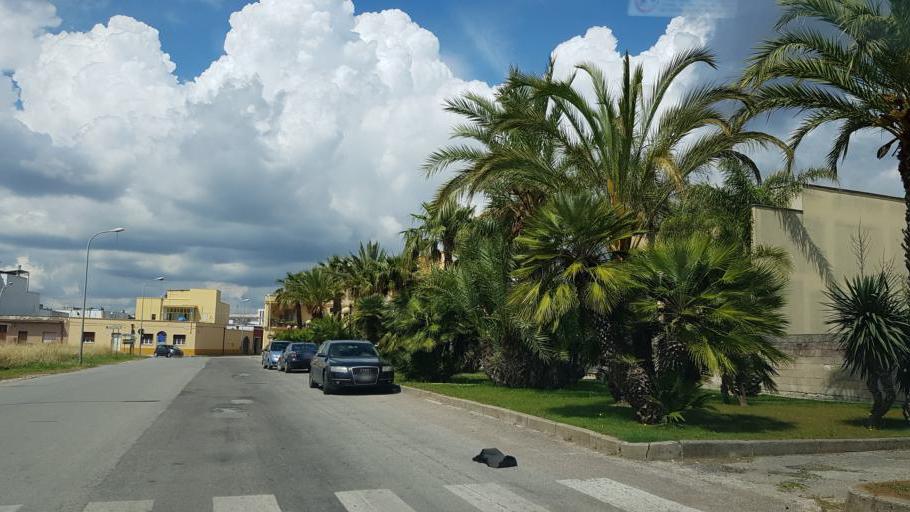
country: IT
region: Apulia
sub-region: Provincia di Brindisi
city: Mesagne
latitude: 40.5512
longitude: 17.8133
